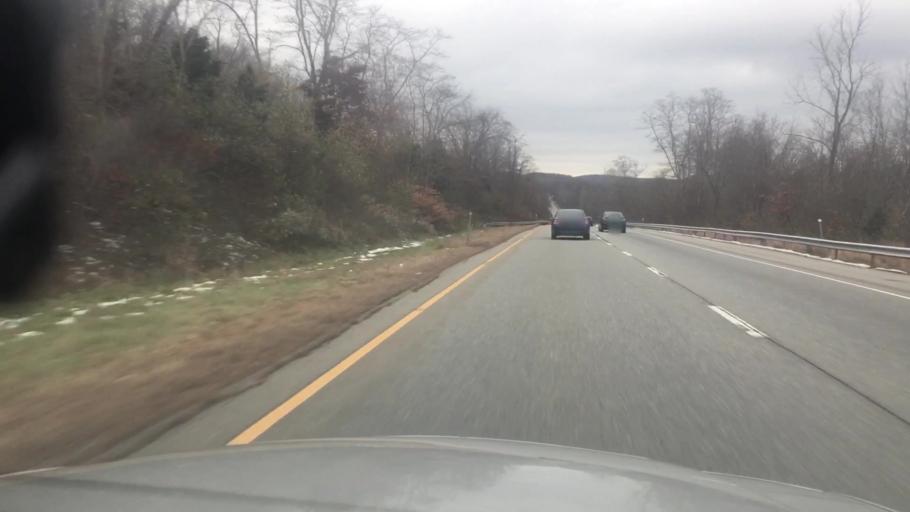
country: US
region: Connecticut
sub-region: Middlesex County
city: Deep River Center
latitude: 41.3802
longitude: -72.4433
